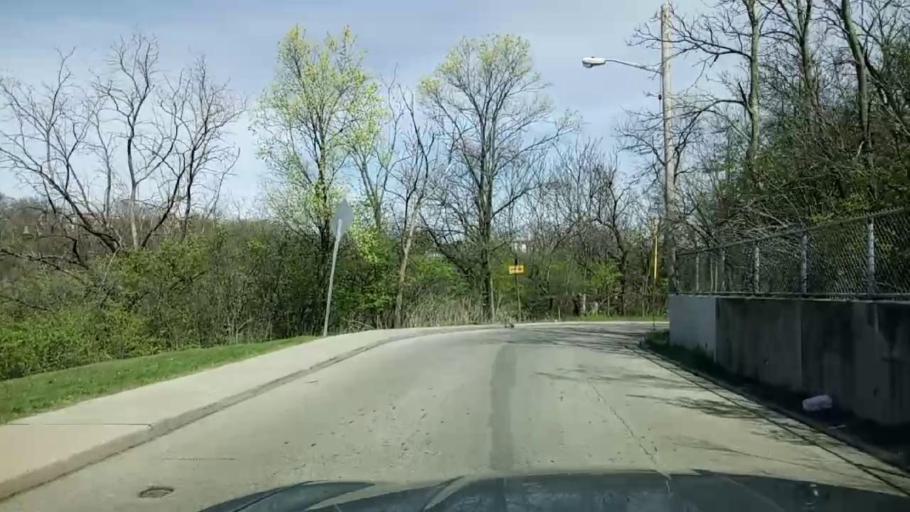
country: US
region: Kentucky
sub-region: Campbell County
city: Newport
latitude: 39.1210
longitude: -84.5138
